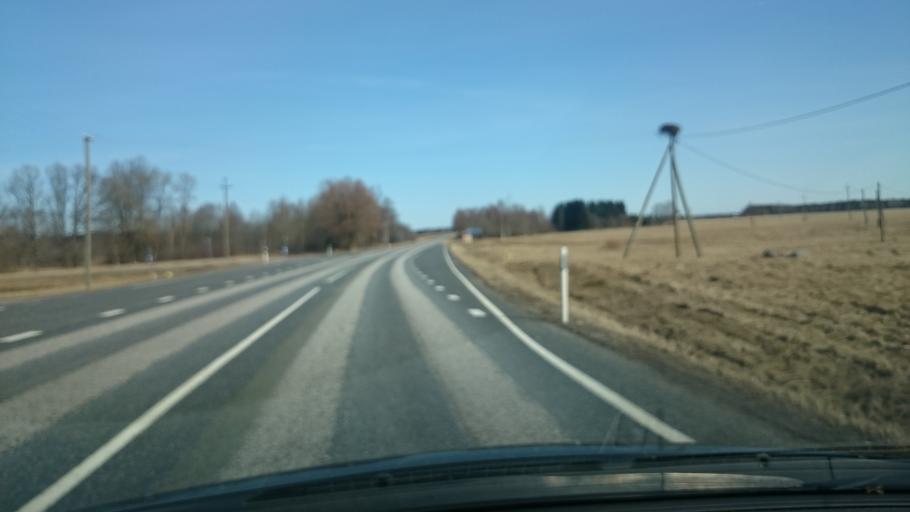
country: EE
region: Jaervamaa
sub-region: Tueri vald
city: Sarevere
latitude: 58.7510
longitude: 25.3226
